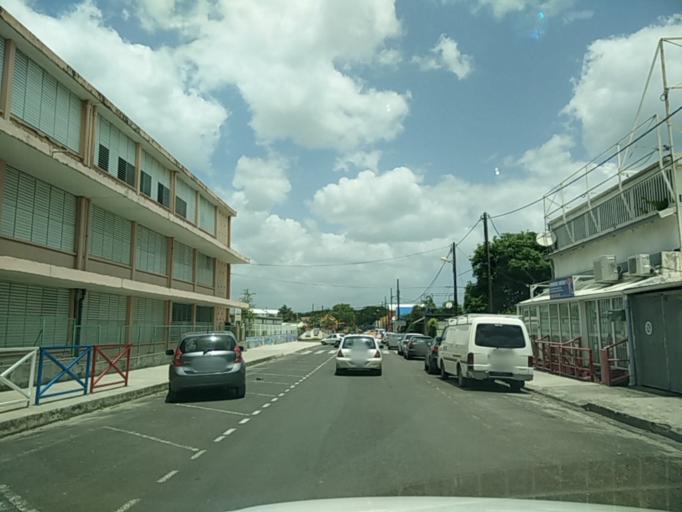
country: GP
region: Guadeloupe
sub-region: Guadeloupe
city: Pointe-a-Pitre
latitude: 16.2597
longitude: -61.5273
